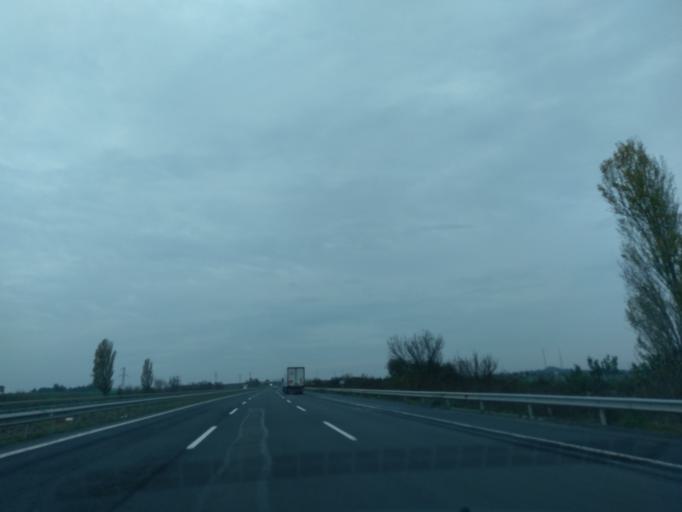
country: TR
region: Istanbul
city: Canta
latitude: 41.1352
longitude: 28.1536
